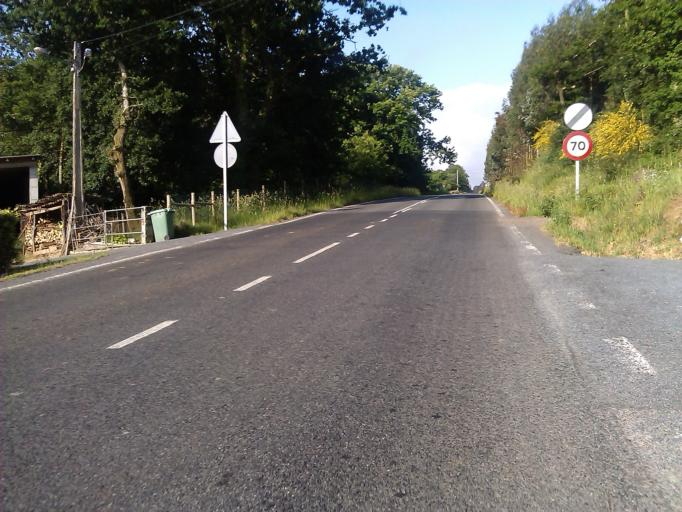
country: ES
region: Galicia
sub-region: Provincia da Coruna
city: Santiso
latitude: 42.9077
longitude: -8.0543
